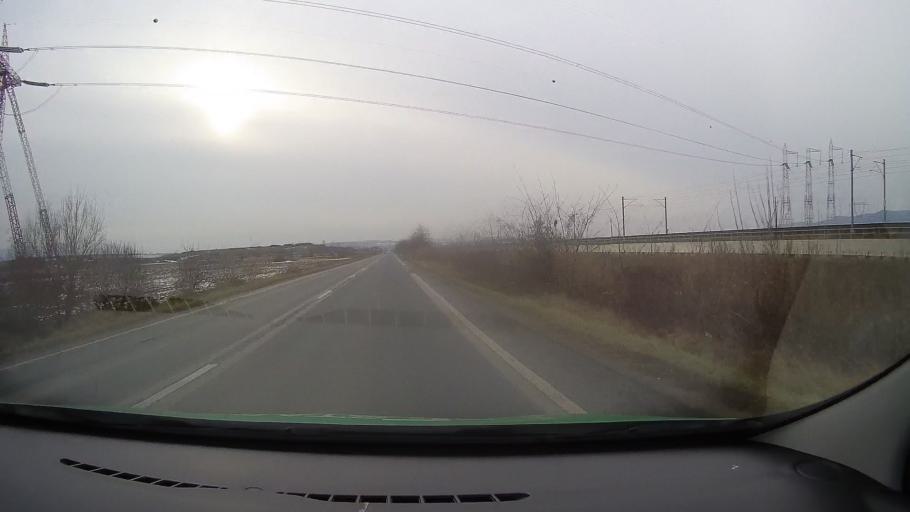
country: RO
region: Hunedoara
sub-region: Municipiul Orastie
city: Orastie
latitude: 45.8748
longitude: 23.2360
